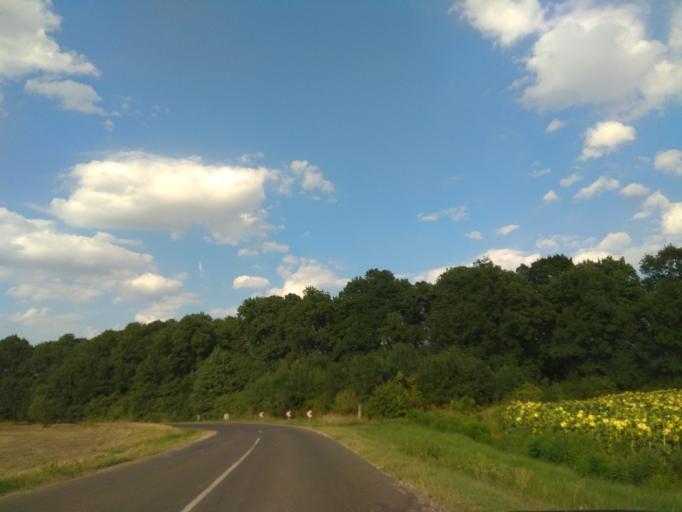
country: HU
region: Borsod-Abauj-Zemplen
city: Harsany
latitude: 47.9398
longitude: 20.7425
